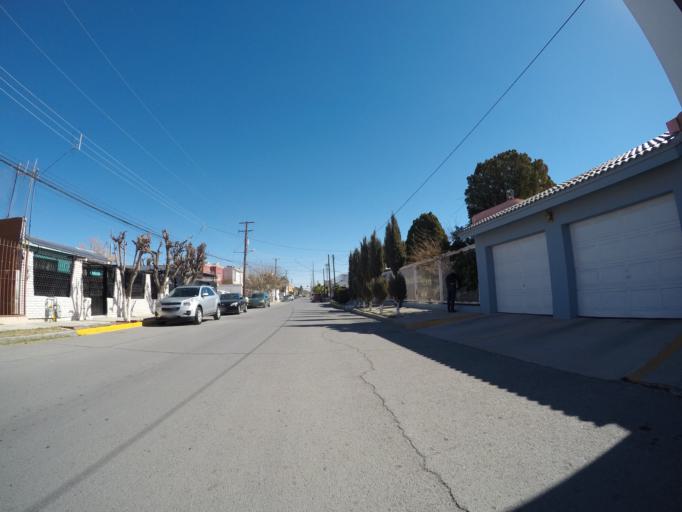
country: MX
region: Chihuahua
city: Ciudad Juarez
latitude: 31.7322
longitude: -106.4426
